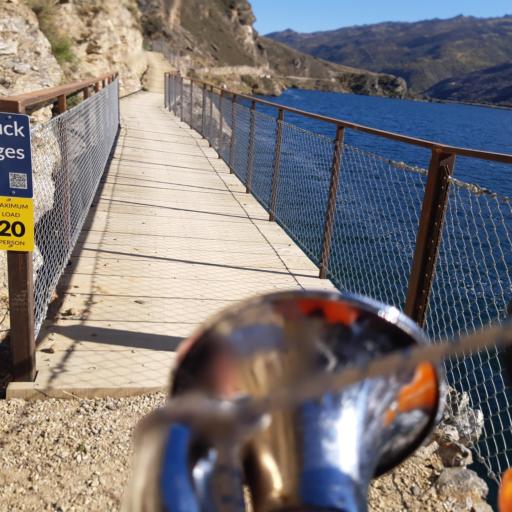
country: NZ
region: Otago
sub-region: Queenstown-Lakes District
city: Wanaka
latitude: -45.1028
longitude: 169.2860
